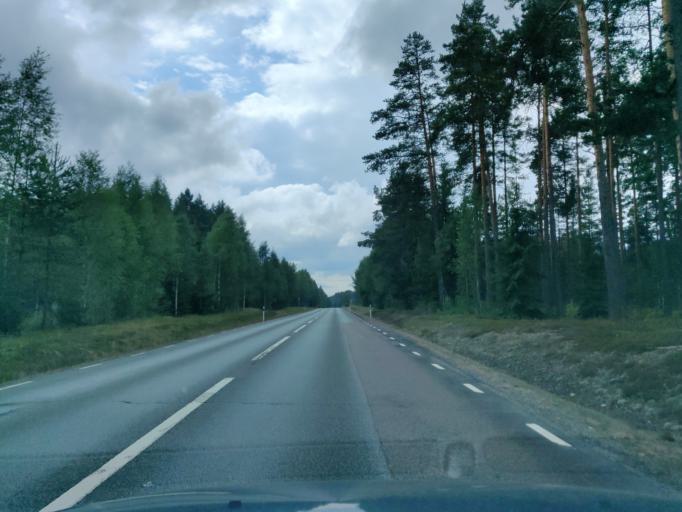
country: SE
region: Vaermland
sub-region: Munkfors Kommun
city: Munkfors
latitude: 59.9276
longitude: 13.5751
